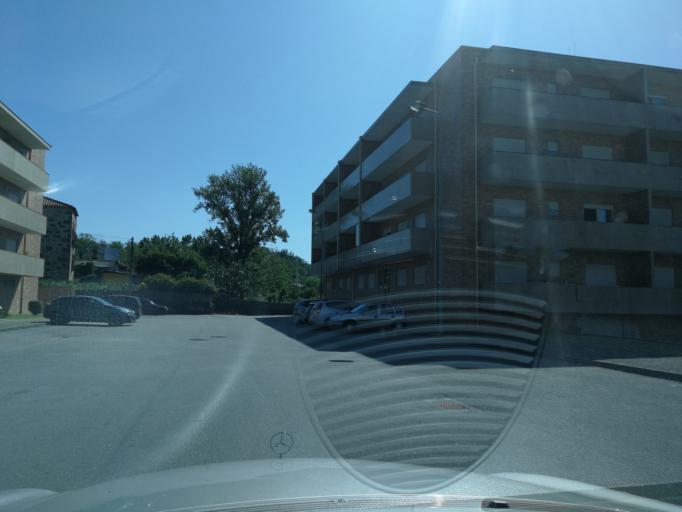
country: PT
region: Braga
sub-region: Braga
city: Adaufe
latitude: 41.5610
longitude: -8.3837
